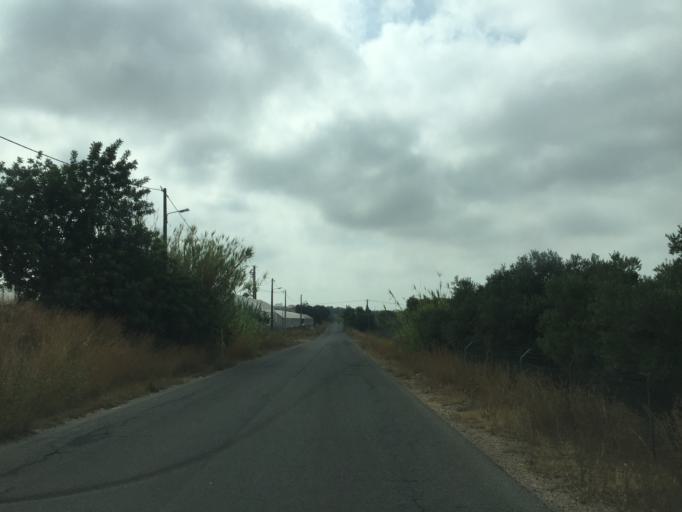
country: PT
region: Faro
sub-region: Olhao
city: Olhao
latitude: 37.0686
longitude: -7.8816
